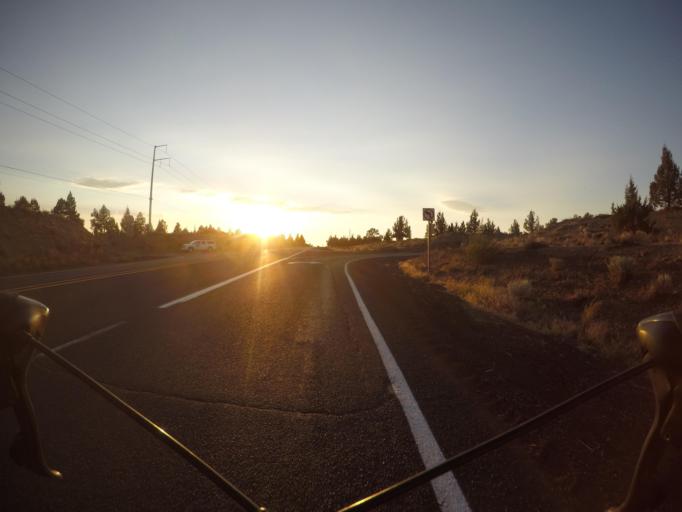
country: US
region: Oregon
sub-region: Deschutes County
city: Redmond
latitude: 44.2760
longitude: -121.2627
